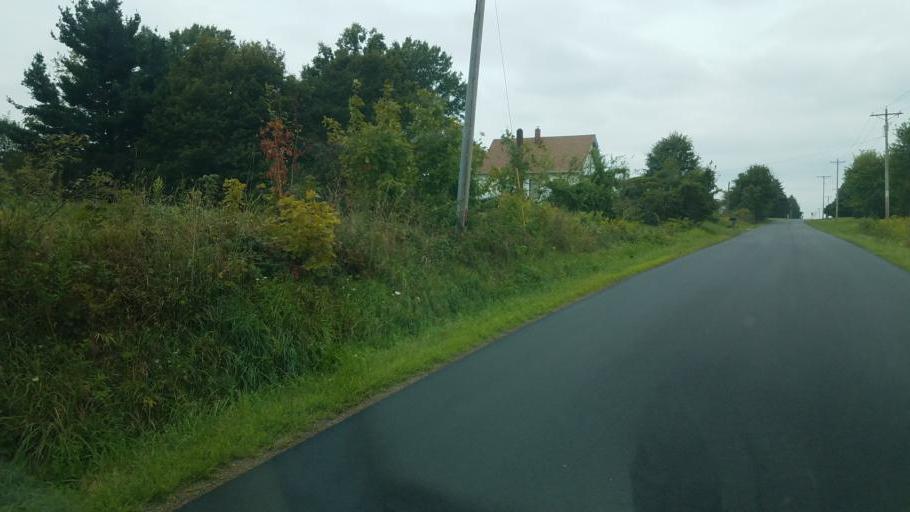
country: US
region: Ohio
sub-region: Morrow County
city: Mount Gilead
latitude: 40.5156
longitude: -82.8047
